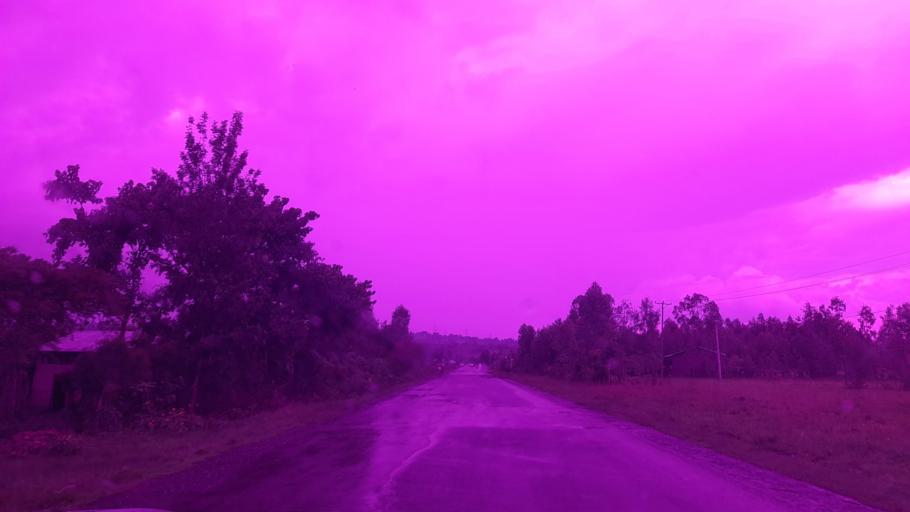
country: ET
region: Oromiya
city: Jima
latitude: 7.7094
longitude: 37.0777
